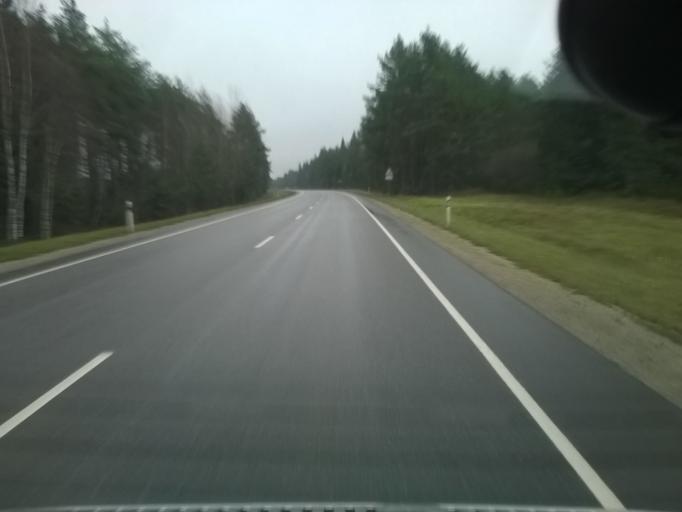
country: EE
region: Harju
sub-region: Nissi vald
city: Turba
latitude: 58.9833
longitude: 23.9939
